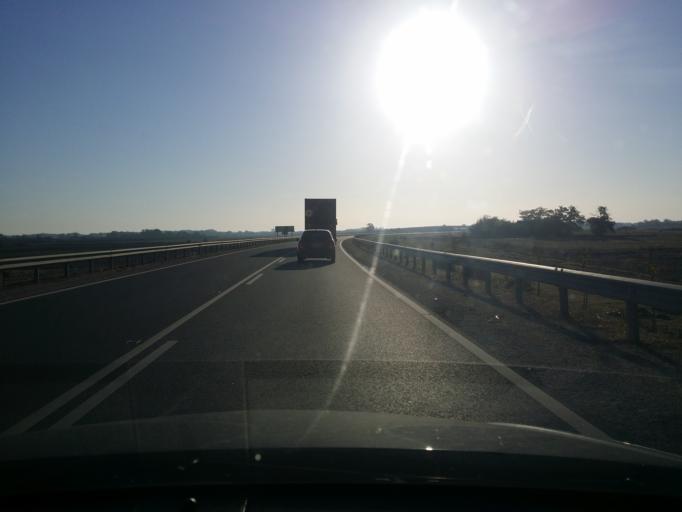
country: HU
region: Bacs-Kiskun
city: Kecskemet
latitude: 46.9503
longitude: 19.6850
